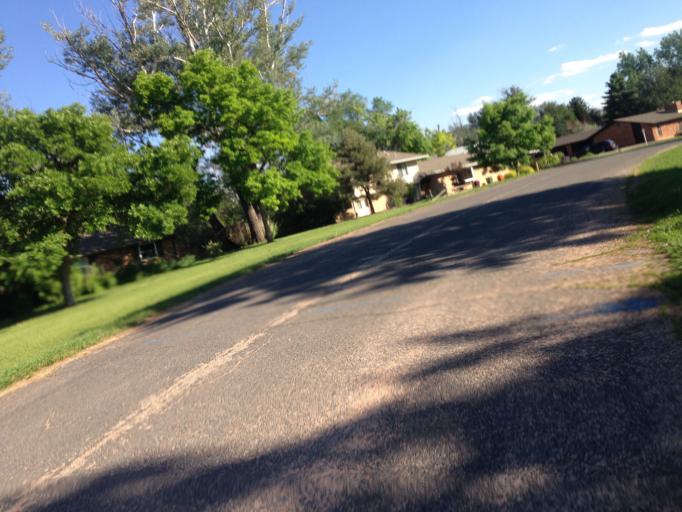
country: US
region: Colorado
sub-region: Boulder County
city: Lafayette
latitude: 40.0181
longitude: -105.1046
